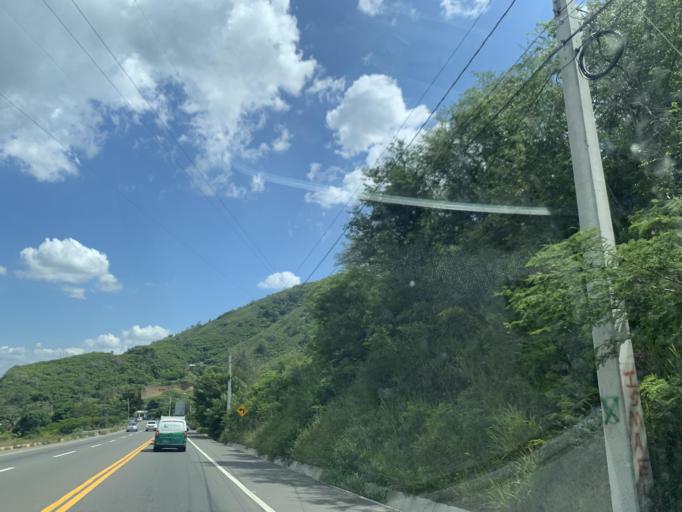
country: DO
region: Santiago
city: Villa Bisono
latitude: 19.6143
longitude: -70.8408
